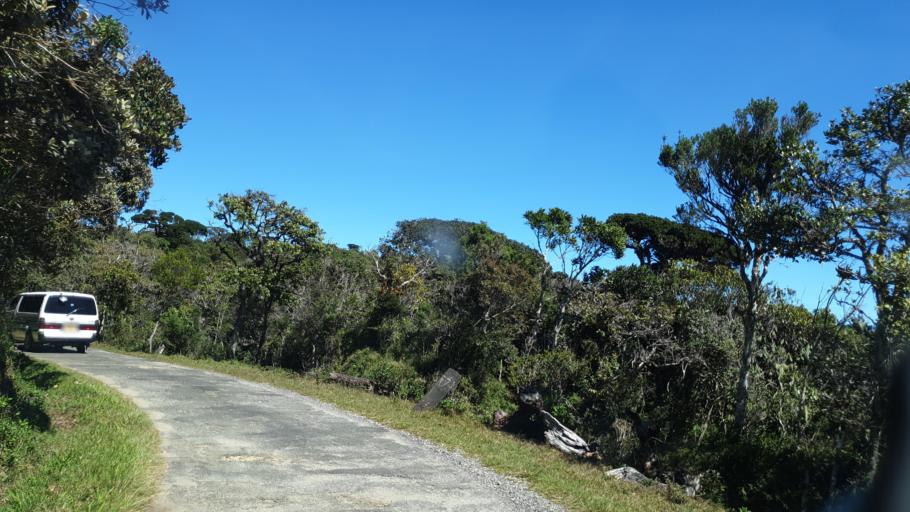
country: LK
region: Uva
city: Haputale
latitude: 6.7972
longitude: 80.8307
